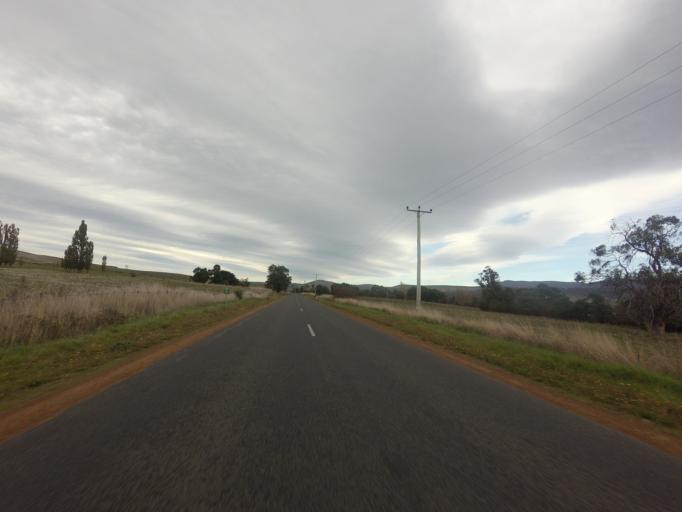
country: AU
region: Tasmania
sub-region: Derwent Valley
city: New Norfolk
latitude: -42.5266
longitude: 146.7510
